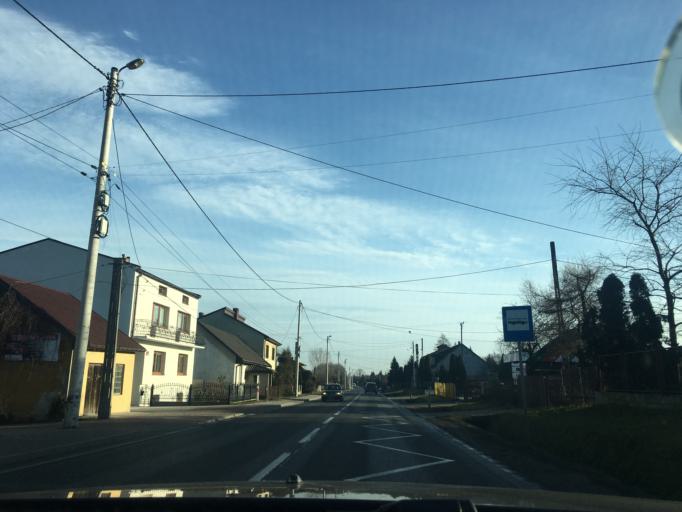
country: PL
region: Swietokrzyskie
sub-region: Powiat jedrzejowski
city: Jedrzejow
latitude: 50.6323
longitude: 20.3233
